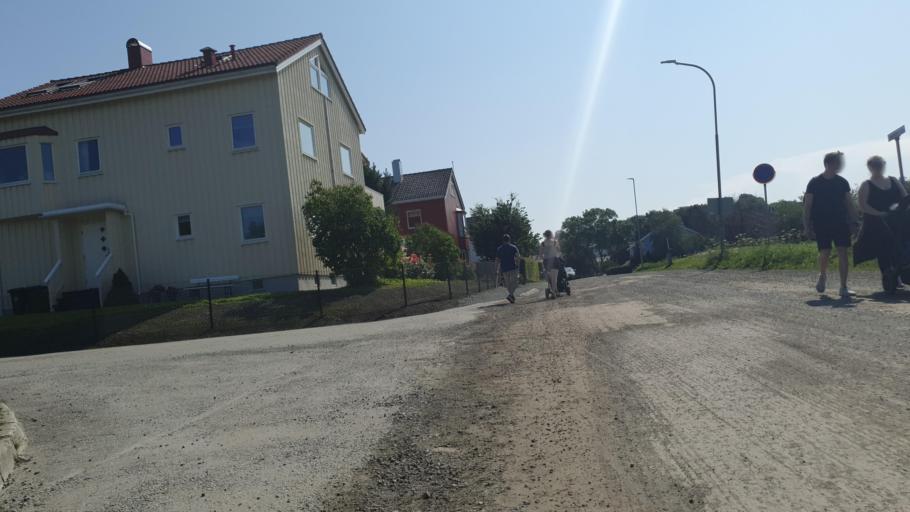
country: NO
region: Sor-Trondelag
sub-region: Trondheim
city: Trondheim
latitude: 63.4508
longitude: 10.4605
